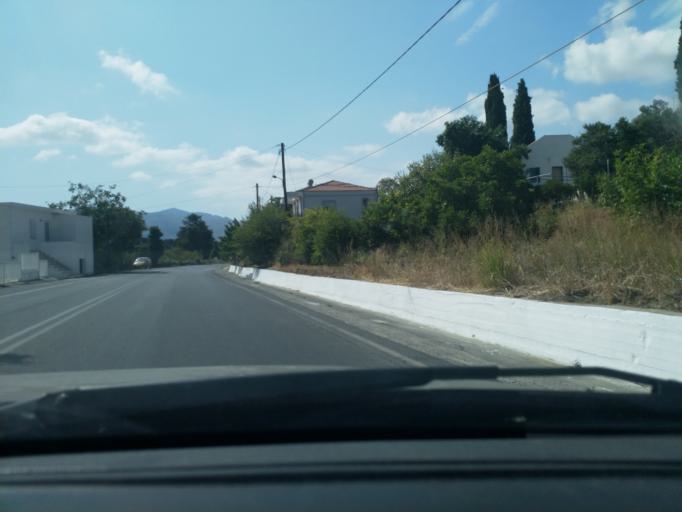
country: GR
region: Crete
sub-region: Nomos Rethymnis
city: Agia Foteini
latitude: 35.2197
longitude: 24.5223
